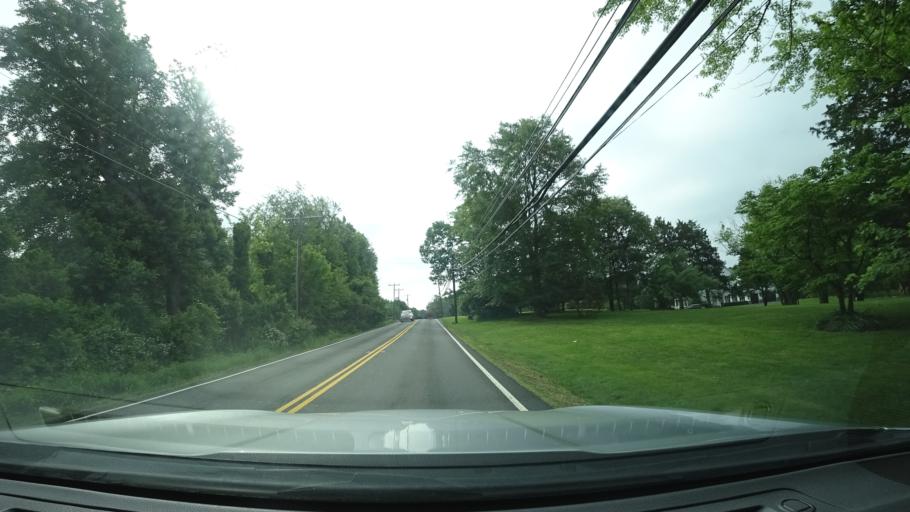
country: US
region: Virginia
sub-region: Fairfax County
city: Great Falls
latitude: 38.9944
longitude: -77.2803
